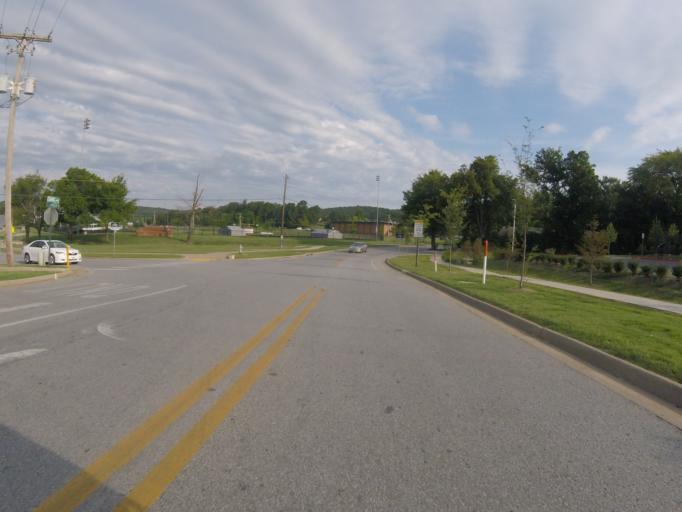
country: US
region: Arkansas
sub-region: Washington County
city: Fayetteville
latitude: 36.0563
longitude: -94.1890
